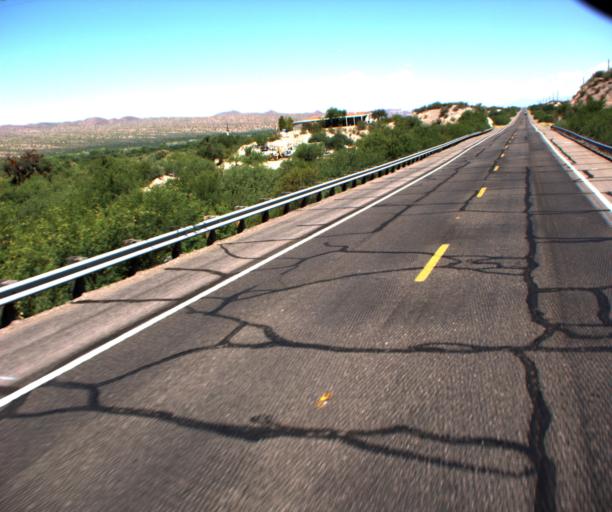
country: US
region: Arizona
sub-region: Pinal County
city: Mammoth
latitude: 32.7780
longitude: -110.6640
